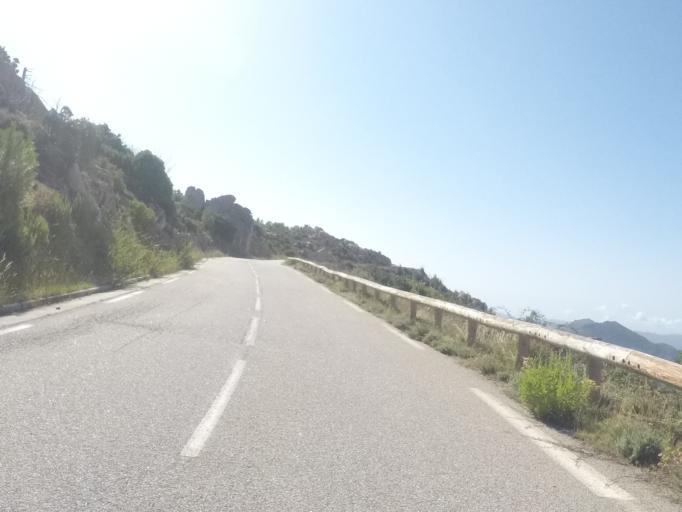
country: FR
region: Corsica
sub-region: Departement de la Corse-du-Sud
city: Olmeto
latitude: 41.7676
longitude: 9.0273
